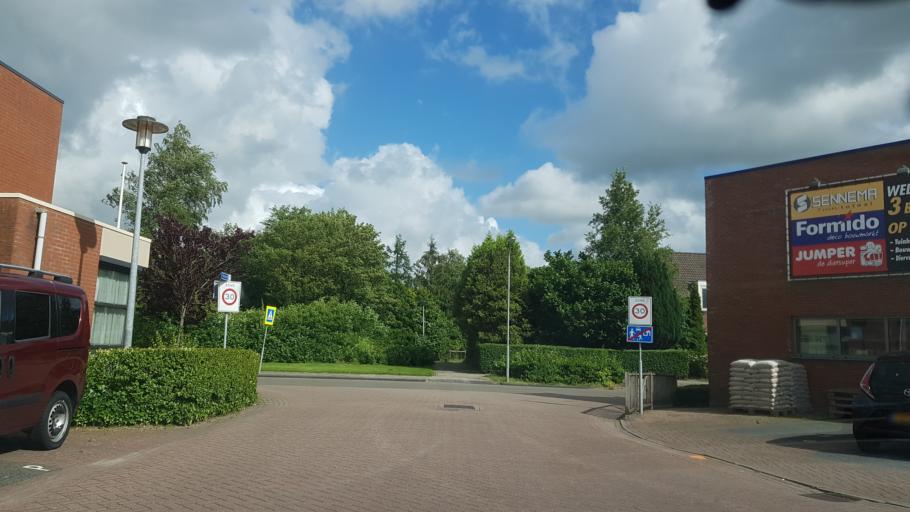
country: NL
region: Groningen
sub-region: Gemeente Bedum
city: Bedum
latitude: 53.4051
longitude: 6.6782
